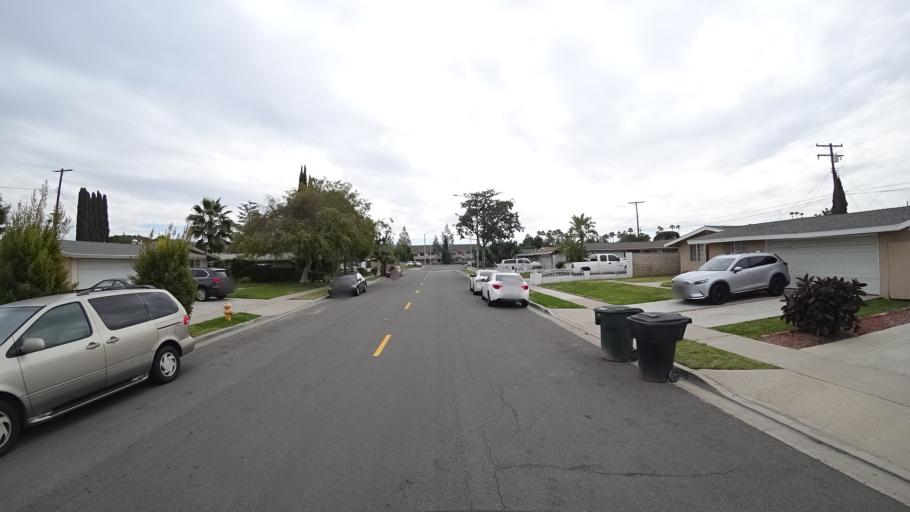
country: US
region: California
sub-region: Orange County
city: Anaheim
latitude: 33.8454
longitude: -117.9356
